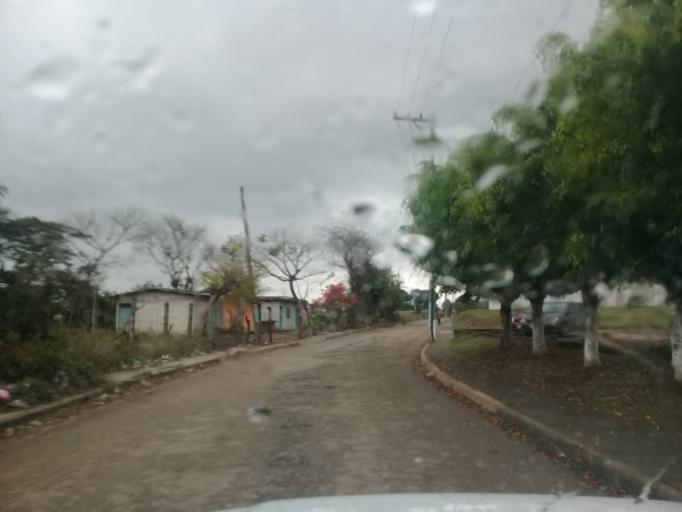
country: MX
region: Veracruz
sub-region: Amatlan de los Reyes
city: Centro de Readaptacion Social
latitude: 18.8390
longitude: -96.9400
